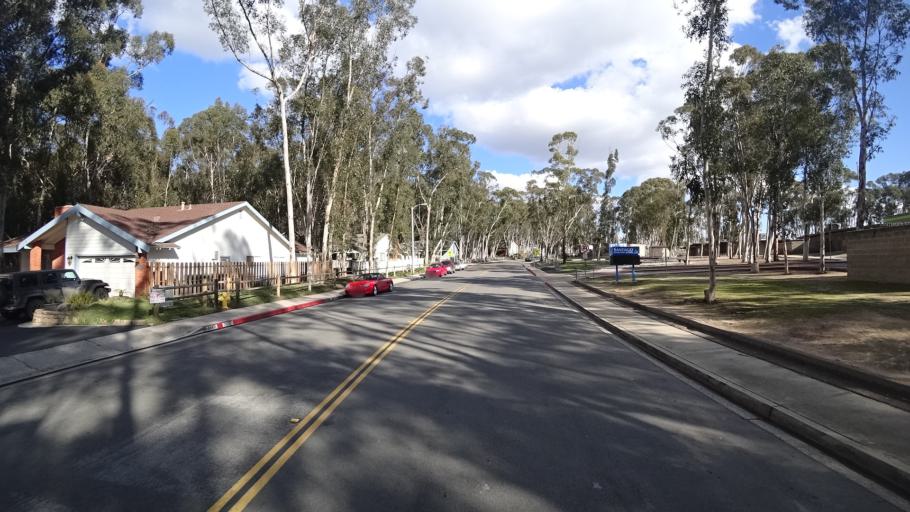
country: US
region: California
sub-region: Orange County
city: Lake Forest
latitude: 33.6333
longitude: -117.6951
